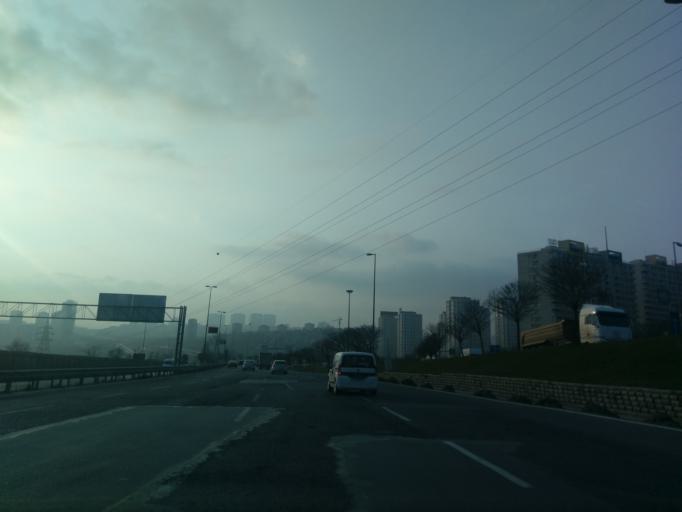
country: TR
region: Istanbul
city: Esenyurt
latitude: 41.0590
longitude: 28.7088
